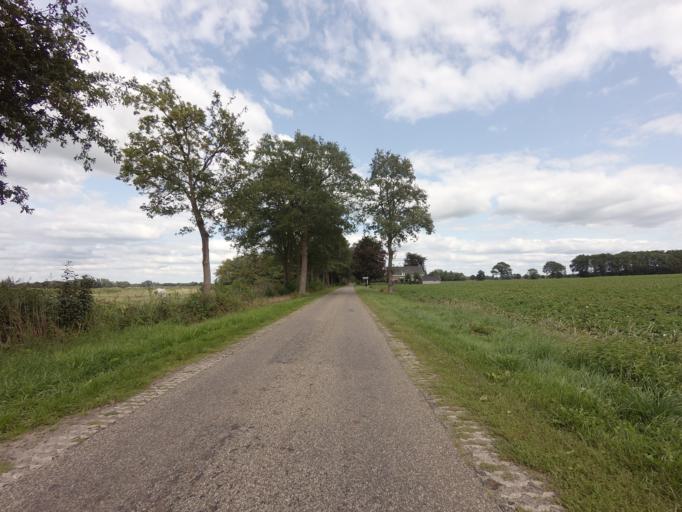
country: NL
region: Drenthe
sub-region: Gemeente De Wolden
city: Ruinen
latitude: 52.7393
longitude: 6.3434
